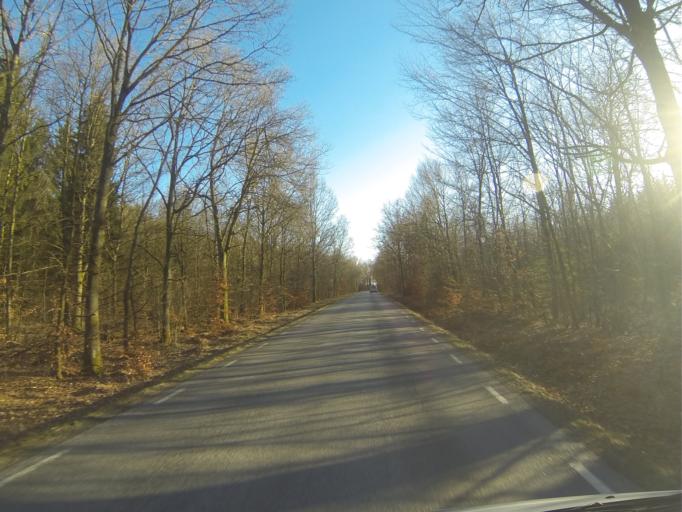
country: SE
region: Skane
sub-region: Horby Kommun
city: Hoerby
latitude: 55.8865
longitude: 13.6650
